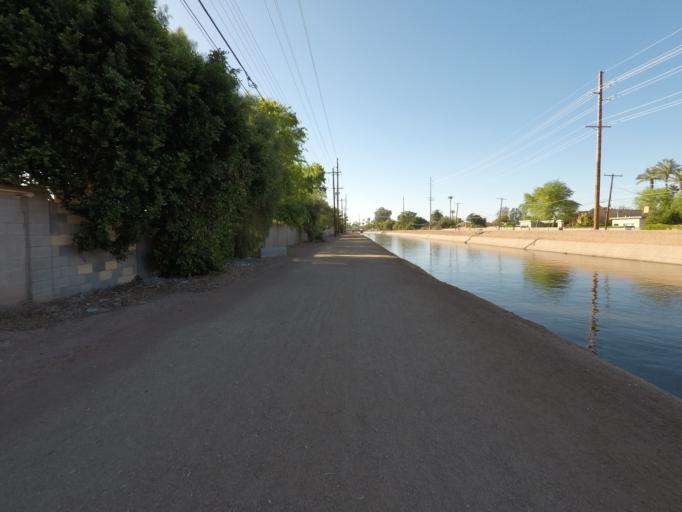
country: US
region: Arizona
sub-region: Maricopa County
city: Paradise Valley
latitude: 33.4983
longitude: -111.9799
